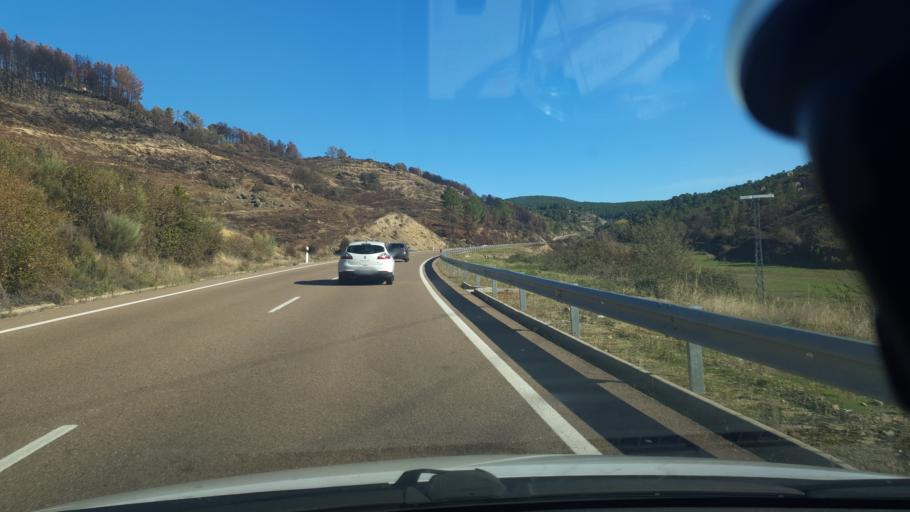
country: ES
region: Castille and Leon
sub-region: Provincia de Avila
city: Poyales del Hoyo
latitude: 40.1628
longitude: -5.1439
